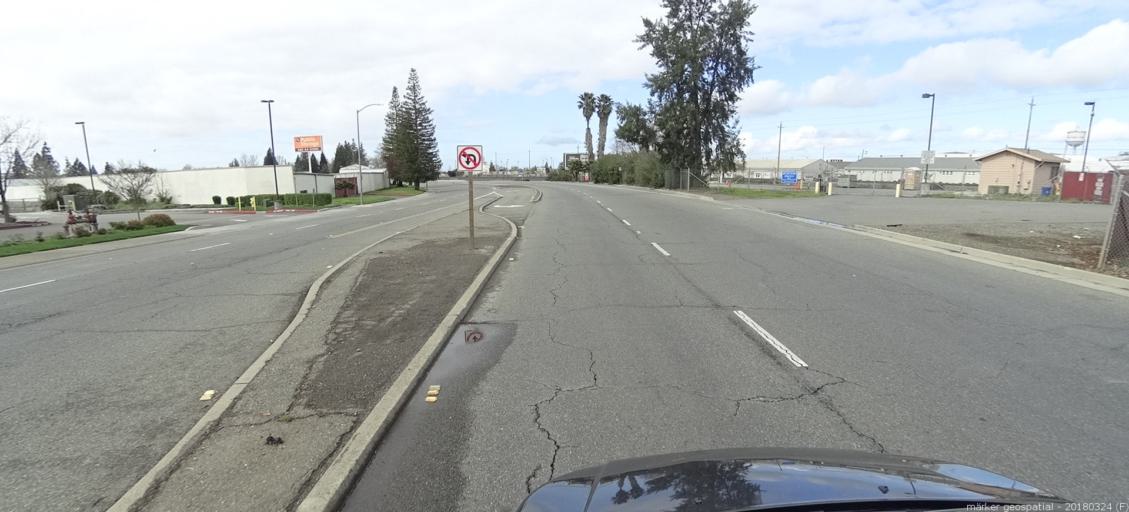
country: US
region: California
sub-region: Sacramento County
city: North Highlands
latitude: 38.6571
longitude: -121.3842
